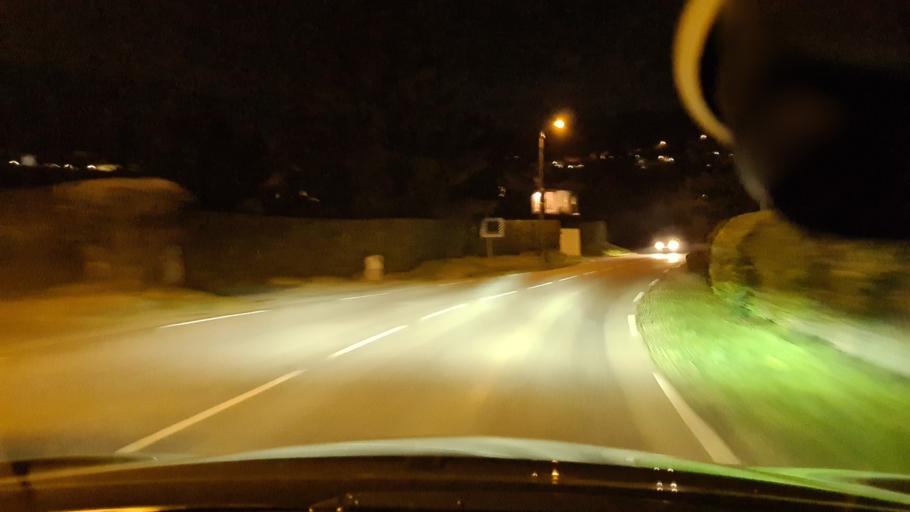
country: FR
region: Rhone-Alpes
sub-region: Departement du Rhone
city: Limonest
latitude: 45.8189
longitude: 4.8078
